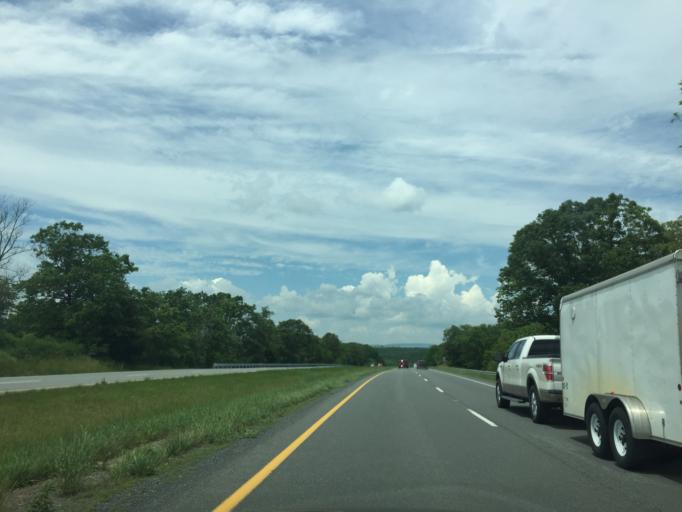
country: US
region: Virginia
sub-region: Frederick County
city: Shawnee Land
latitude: 39.2766
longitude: -78.2539
